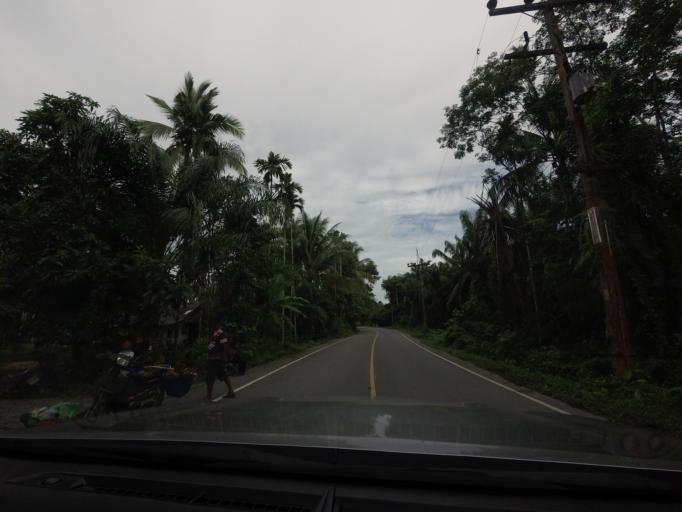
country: TH
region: Nakhon Si Thammarat
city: Phra Phrom
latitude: 8.2827
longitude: 99.9335
